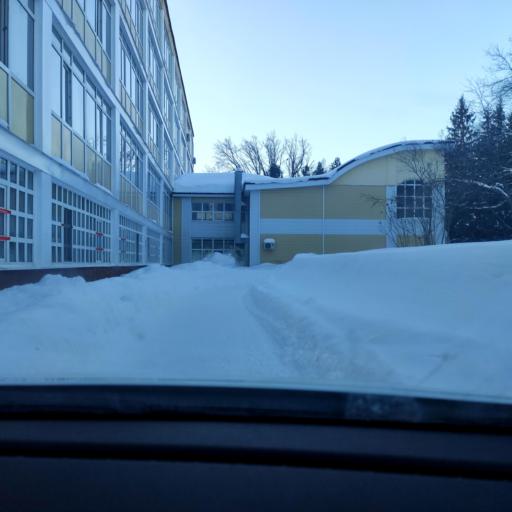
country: RU
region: Bashkortostan
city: Ufa
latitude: 54.7137
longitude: 56.0164
